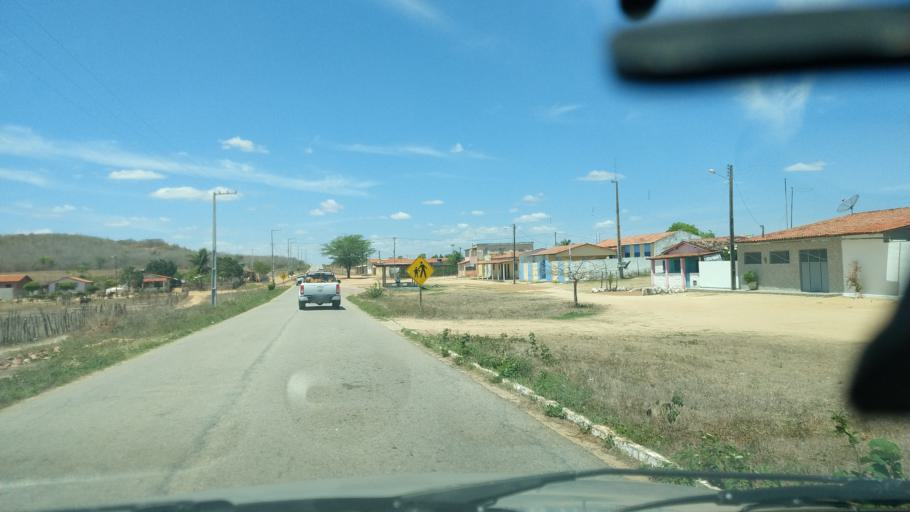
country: BR
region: Rio Grande do Norte
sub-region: Sao Paulo Do Potengi
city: Sao Paulo do Potengi
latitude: -5.9180
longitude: -35.5854
